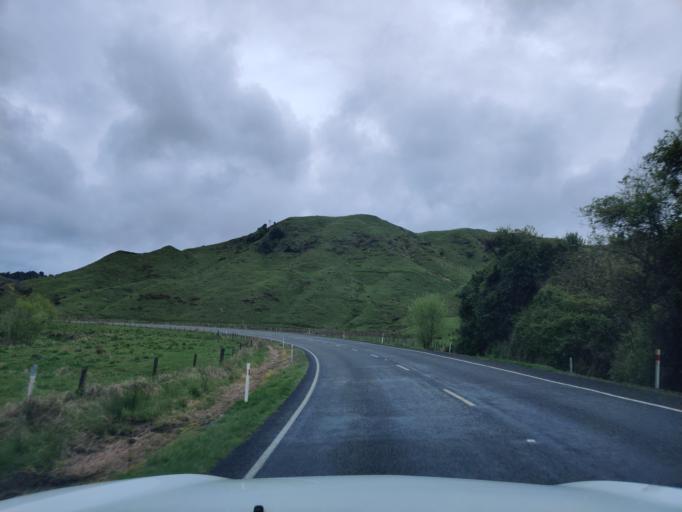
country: NZ
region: Waikato
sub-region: Otorohanga District
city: Otorohanga
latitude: -38.5517
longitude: 175.1956
